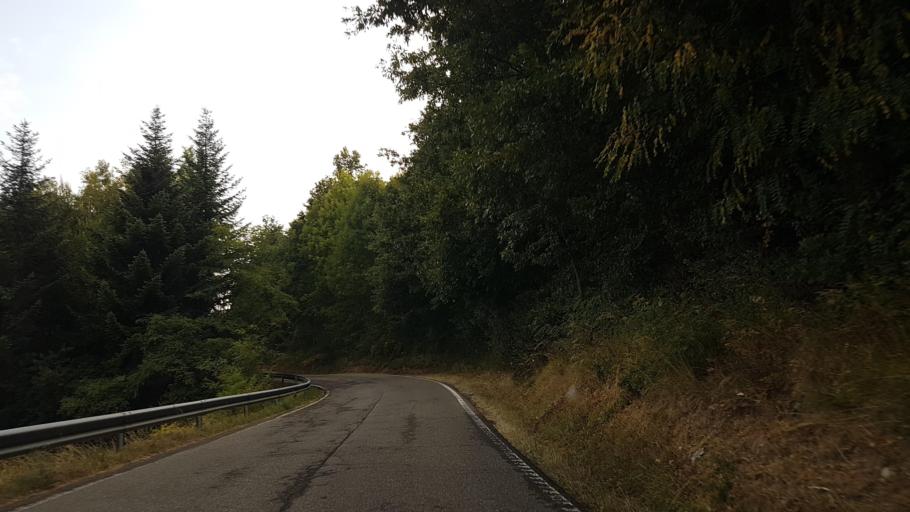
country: IT
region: Emilia-Romagna
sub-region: Provincia di Parma
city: Albareto
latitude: 44.4641
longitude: 9.6991
